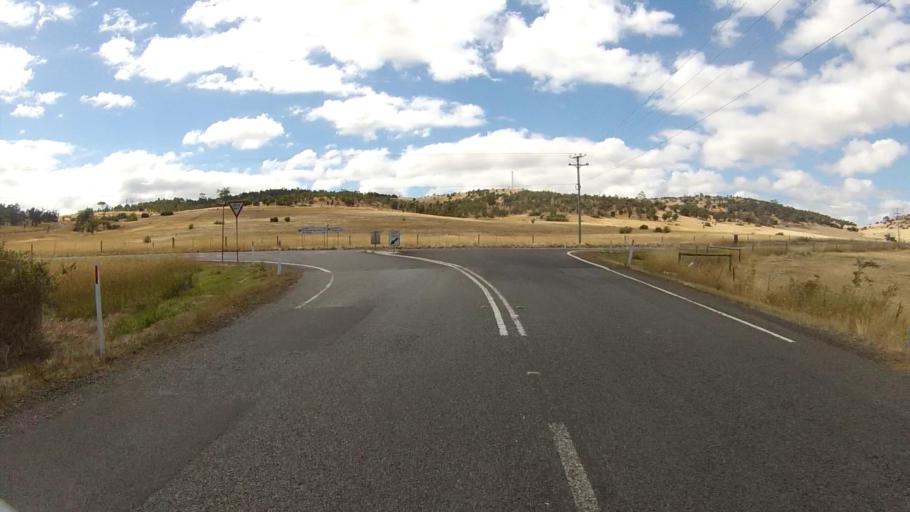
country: AU
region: Tasmania
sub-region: Sorell
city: Sorell
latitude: -42.7615
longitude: 147.5423
